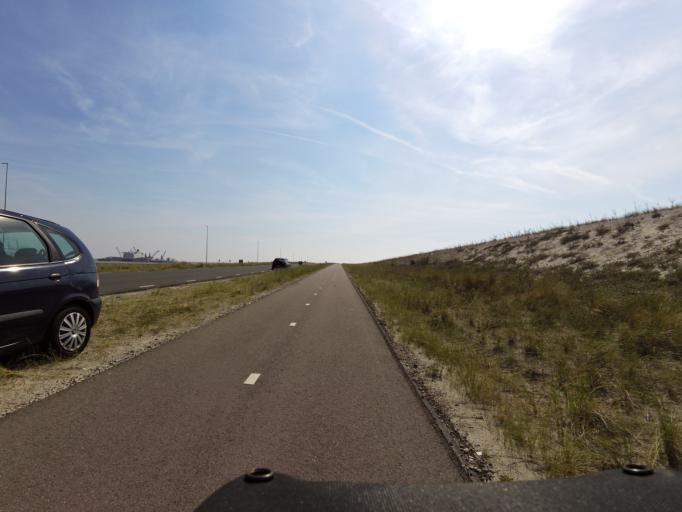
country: NL
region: South Holland
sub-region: Gemeente Rotterdam
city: Hoek van Holland
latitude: 51.9780
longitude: 3.9776
